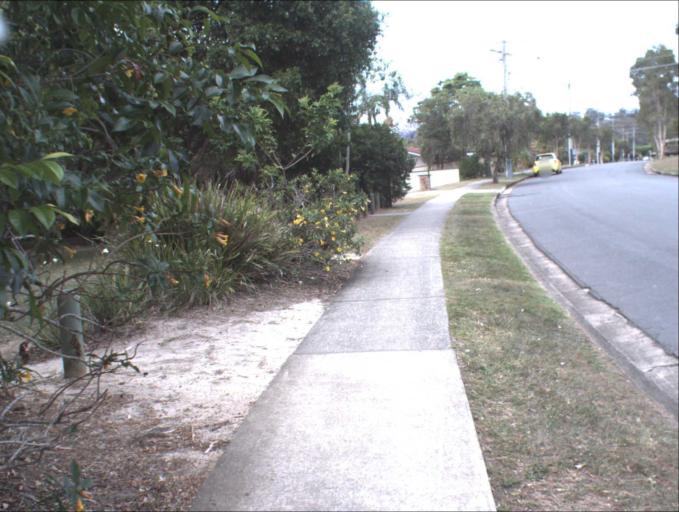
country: AU
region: Queensland
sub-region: Logan
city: Springwood
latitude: -27.6222
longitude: 153.1293
